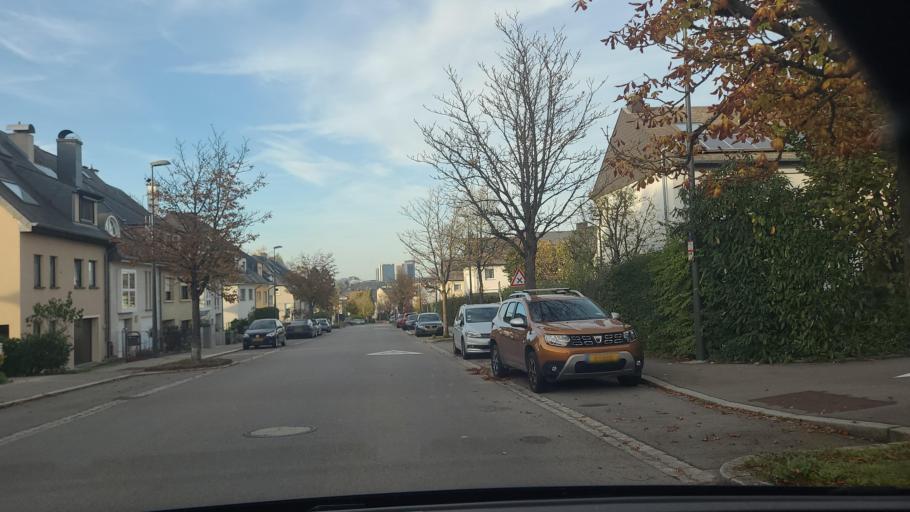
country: LU
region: Luxembourg
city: Itzig
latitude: 49.5943
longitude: 6.1507
